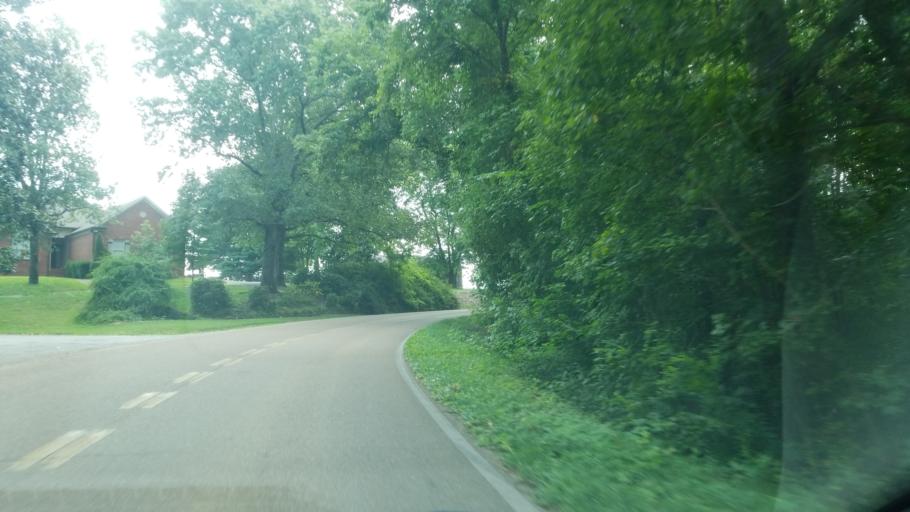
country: US
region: Tennessee
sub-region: Hamilton County
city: Lakesite
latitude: 35.2086
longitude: -85.0814
